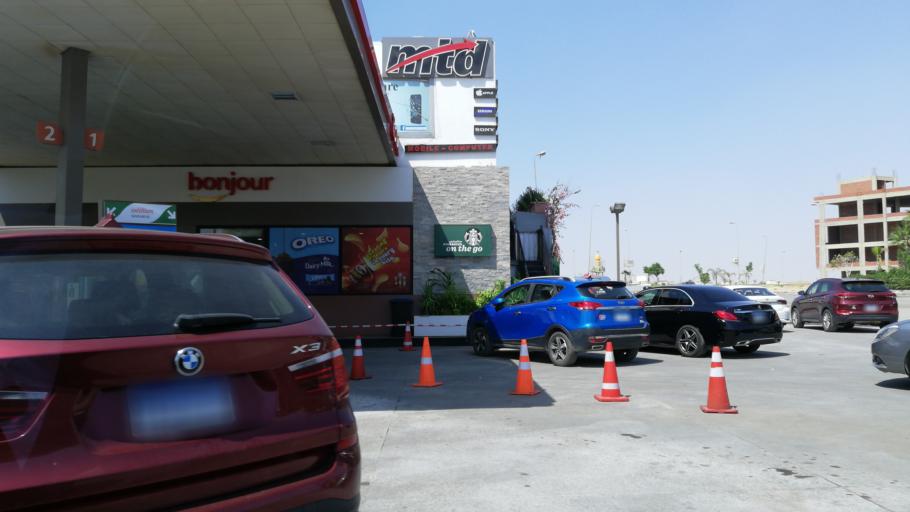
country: EG
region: Muhafazat al Qalyubiyah
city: Al Khankah
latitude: 30.0258
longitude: 31.4889
